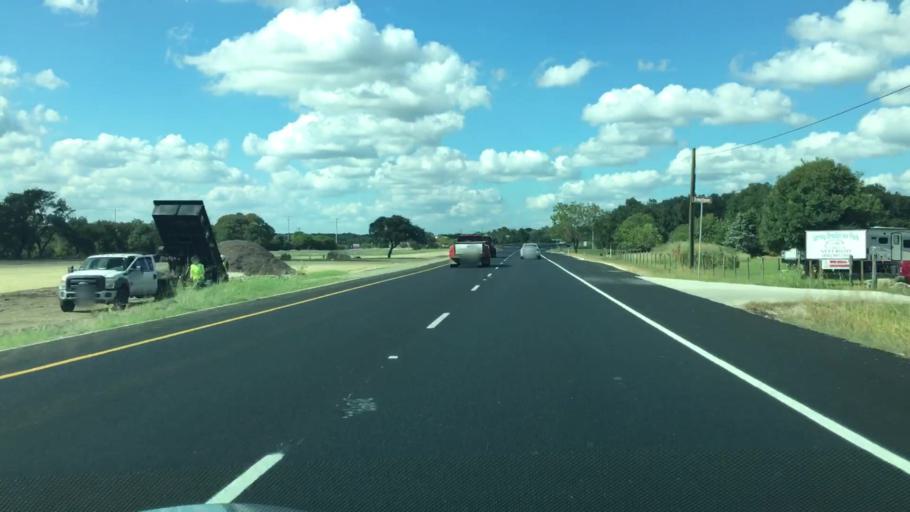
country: US
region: Texas
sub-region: Comal County
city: Canyon Lake
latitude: 29.8928
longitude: -98.4091
